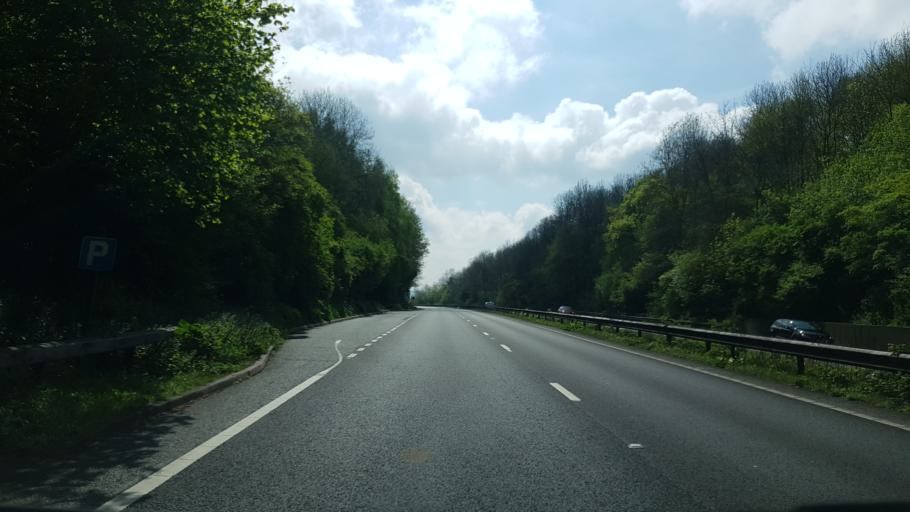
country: GB
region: England
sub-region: Kent
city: Sevenoaks
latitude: 51.2516
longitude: 0.1769
